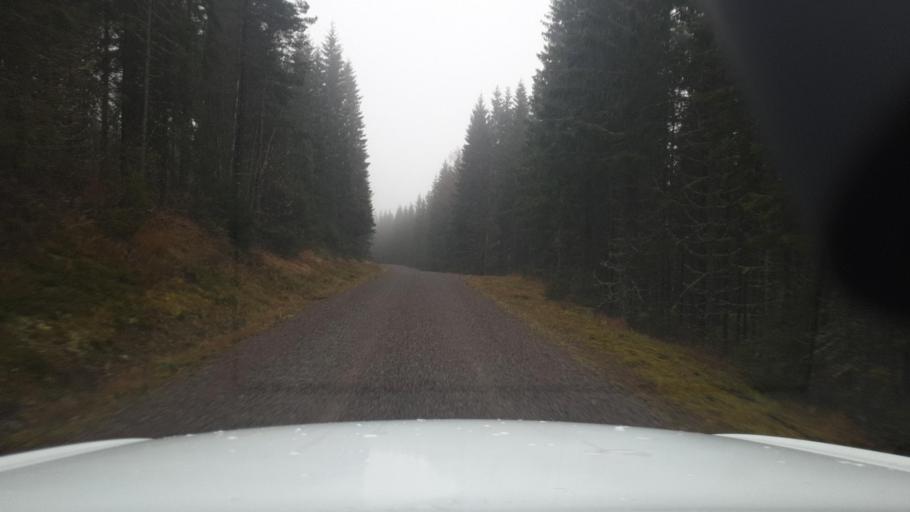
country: SE
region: Vaermland
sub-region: Eda Kommun
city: Charlottenberg
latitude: 60.0875
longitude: 12.6171
